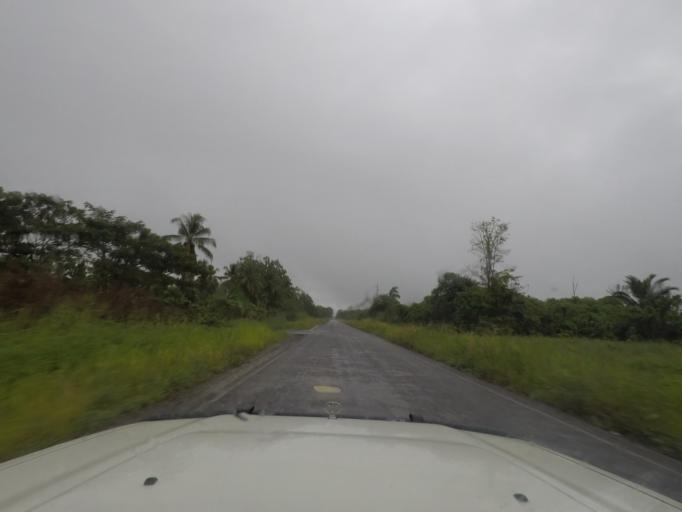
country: PG
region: Madang
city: Madang
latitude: -5.3820
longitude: 145.6953
